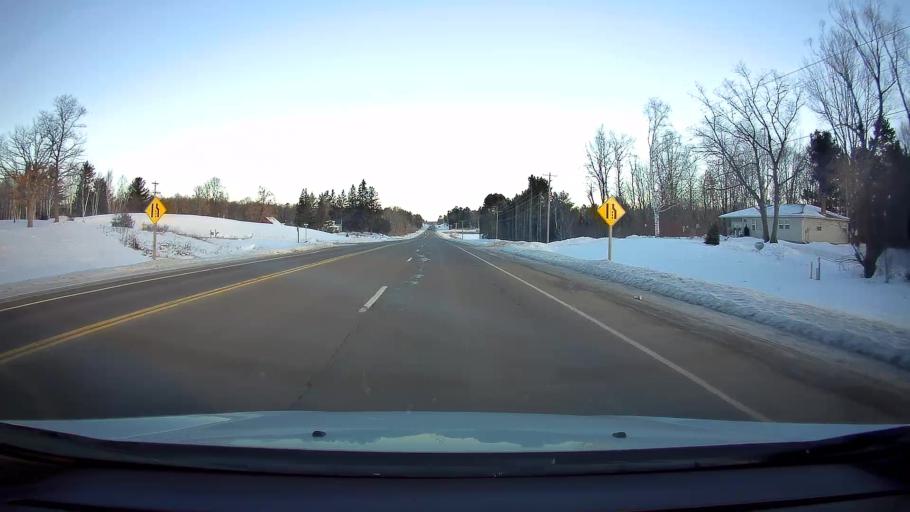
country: US
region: Wisconsin
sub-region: Barron County
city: Cumberland
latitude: 45.5739
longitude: -92.0174
